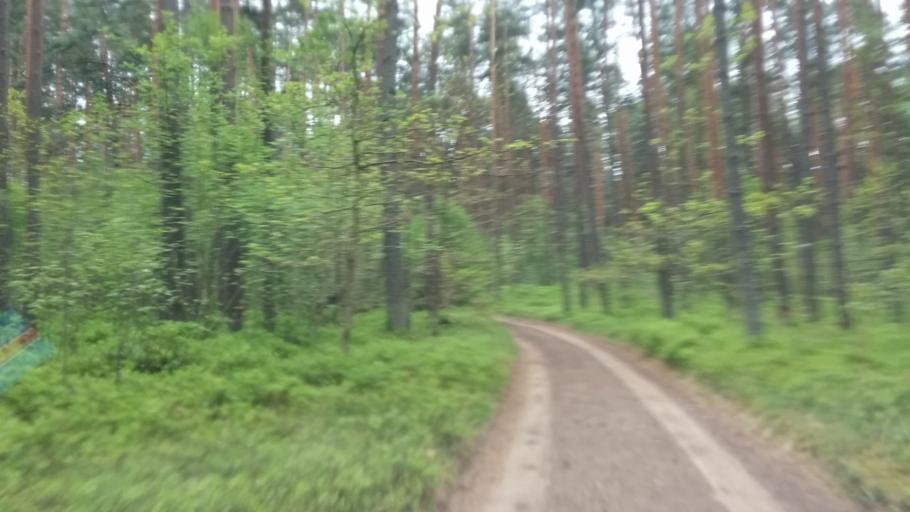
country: LV
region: Babite
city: Pinki
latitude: 56.9397
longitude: 23.9245
